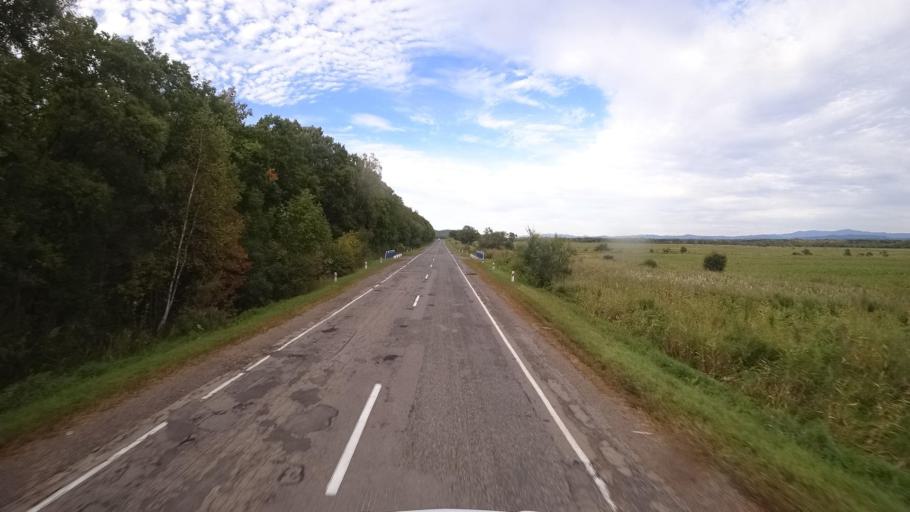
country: RU
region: Primorskiy
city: Dostoyevka
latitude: 44.3566
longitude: 133.4274
